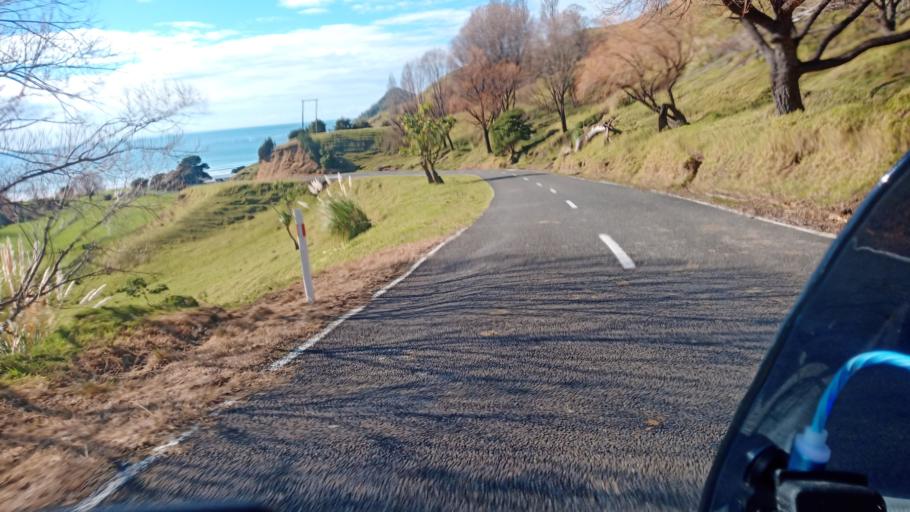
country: NZ
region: Gisborne
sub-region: Gisborne District
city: Gisborne
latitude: -38.2488
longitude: 178.3117
